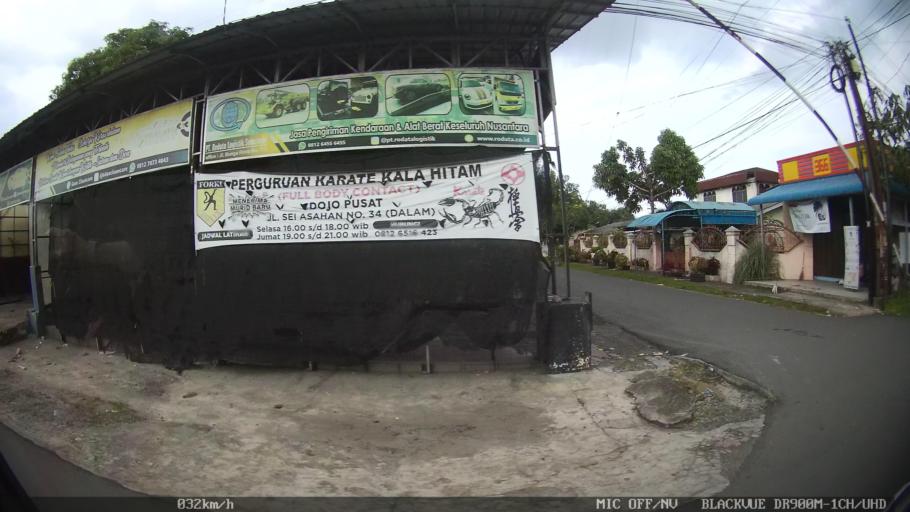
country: ID
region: North Sumatra
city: Sunggal
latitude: 3.5248
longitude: 98.6137
